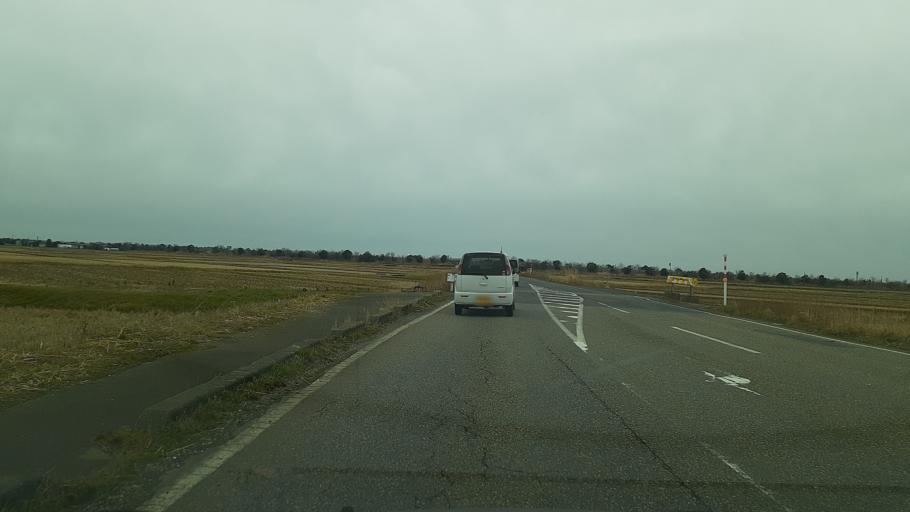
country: JP
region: Niigata
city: Niitsu-honcho
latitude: 37.8165
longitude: 139.0842
